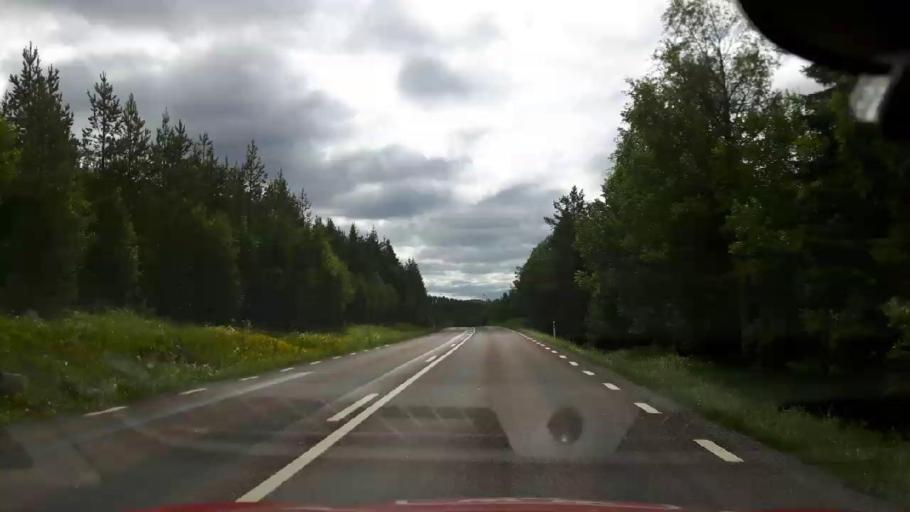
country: SE
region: Jaemtland
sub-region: OEstersunds Kommun
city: Brunflo
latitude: 62.9955
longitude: 14.9710
